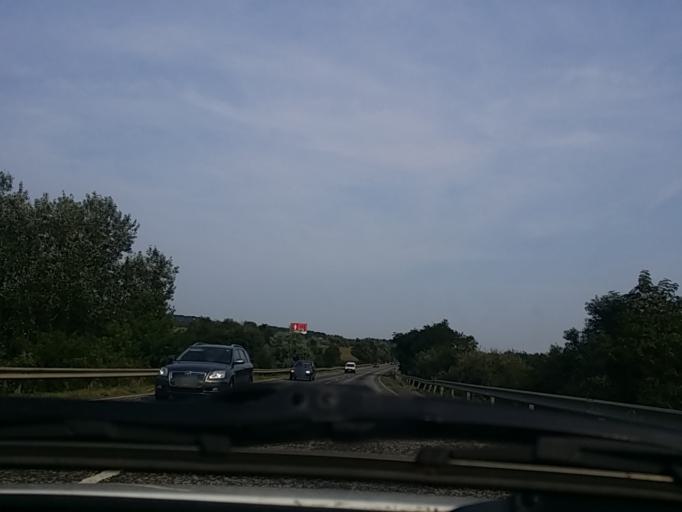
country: HU
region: Pest
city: Biatorbagy
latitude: 47.4902
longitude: 18.8233
